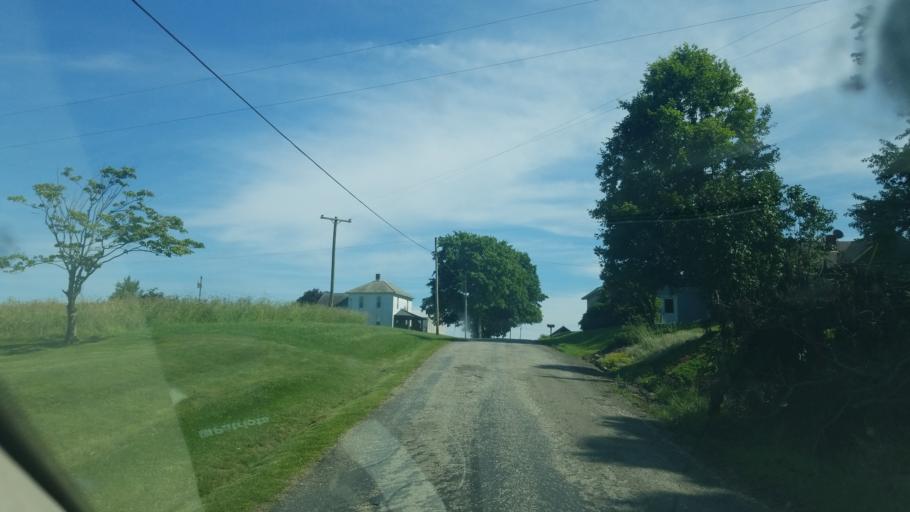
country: US
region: Ohio
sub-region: Holmes County
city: Millersburg
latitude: 40.4799
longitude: -81.9632
